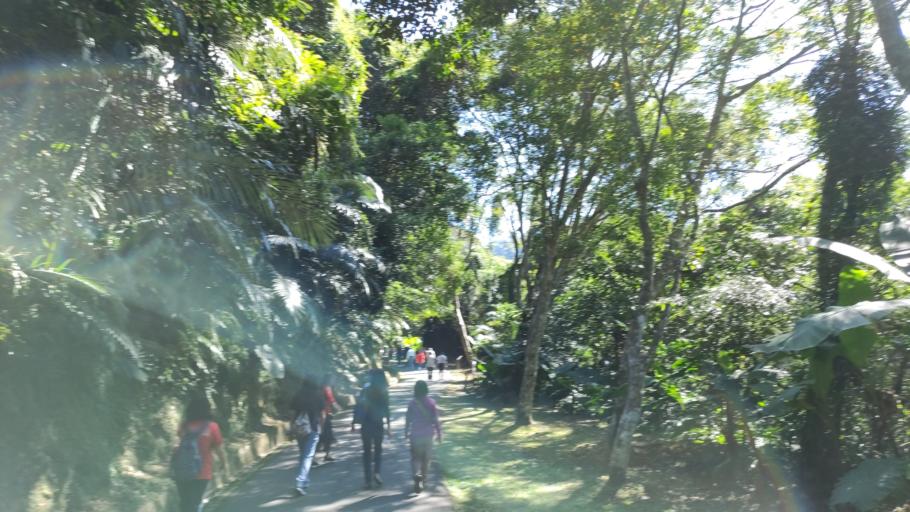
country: TW
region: Taiwan
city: Daxi
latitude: 24.8419
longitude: 121.3051
